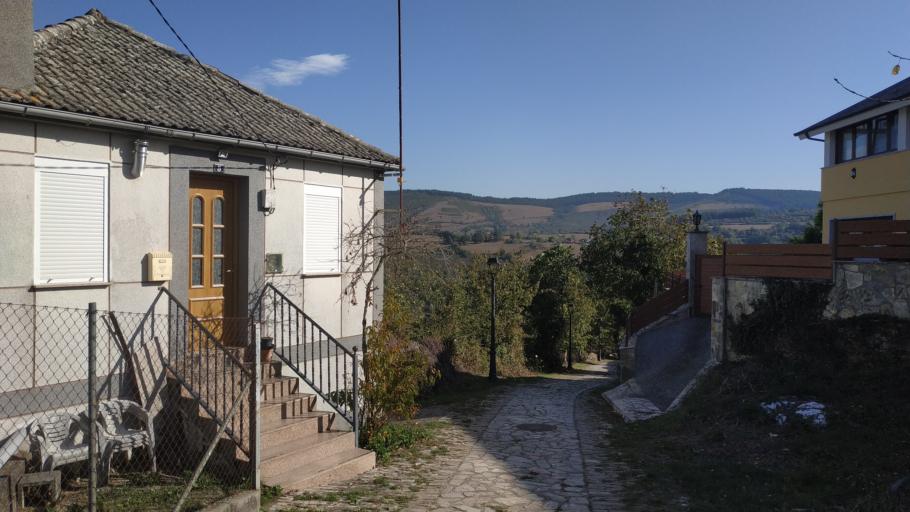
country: ES
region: Galicia
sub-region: Provincia de Lugo
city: San Roman
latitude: 42.8731
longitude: -7.0631
